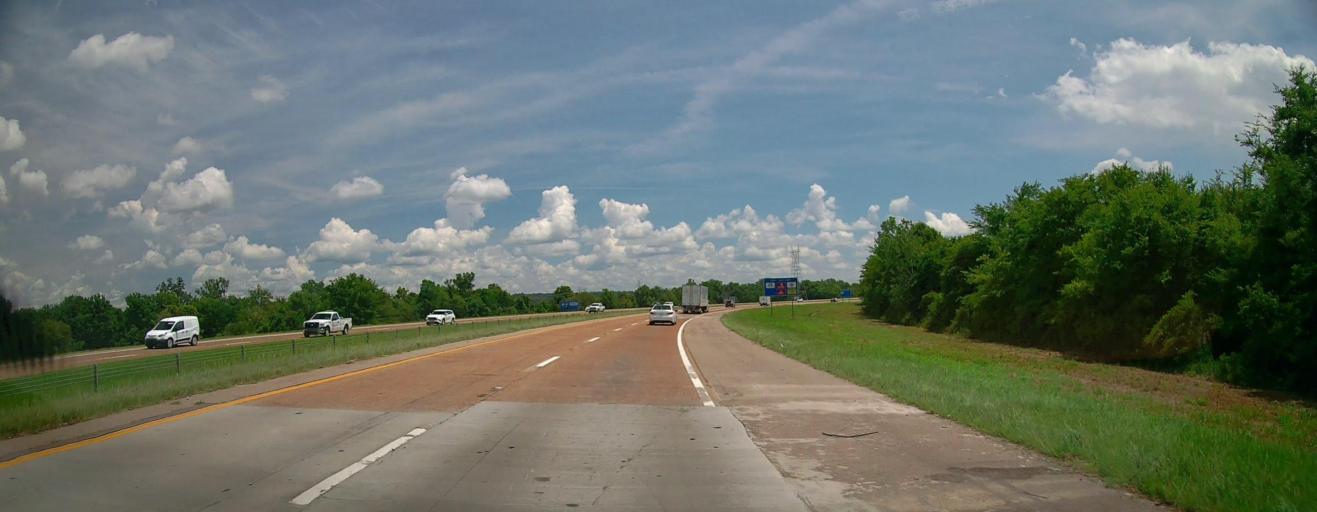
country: US
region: Mississippi
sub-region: Lee County
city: Tupelo
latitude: 34.2682
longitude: -88.6961
